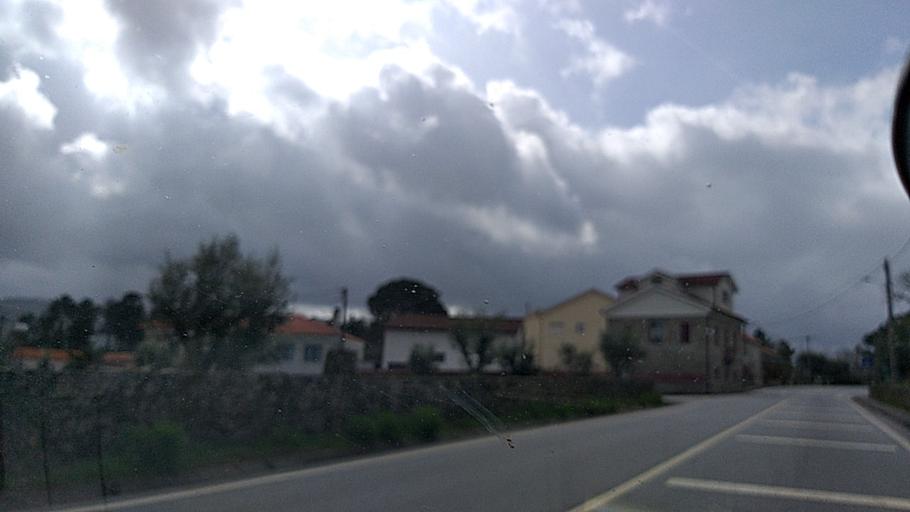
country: PT
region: Viseu
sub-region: Mangualde
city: Mangualde
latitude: 40.6296
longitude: -7.7487
